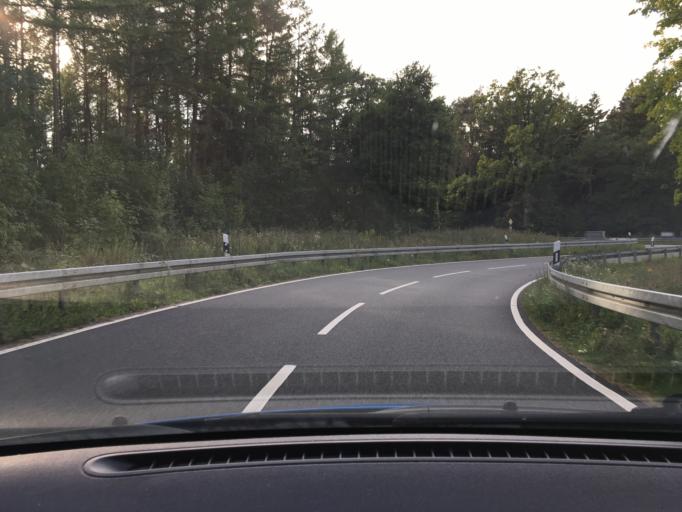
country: DE
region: Lower Saxony
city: Fassberg
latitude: 52.9072
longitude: 10.0945
